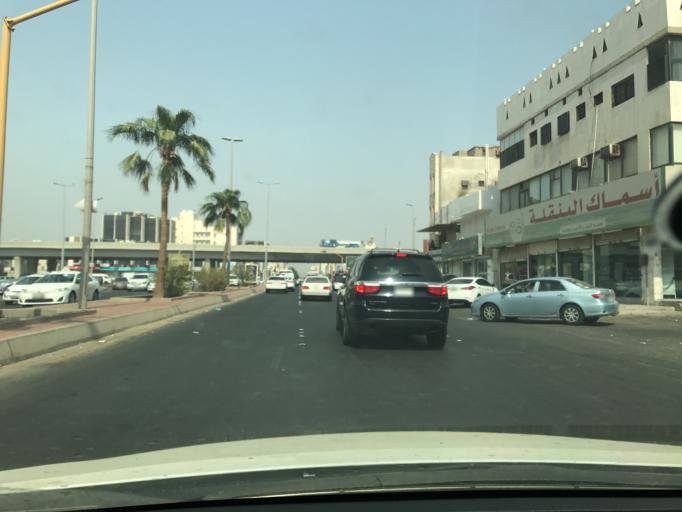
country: SA
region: Makkah
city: Jeddah
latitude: 21.6157
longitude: 39.1653
